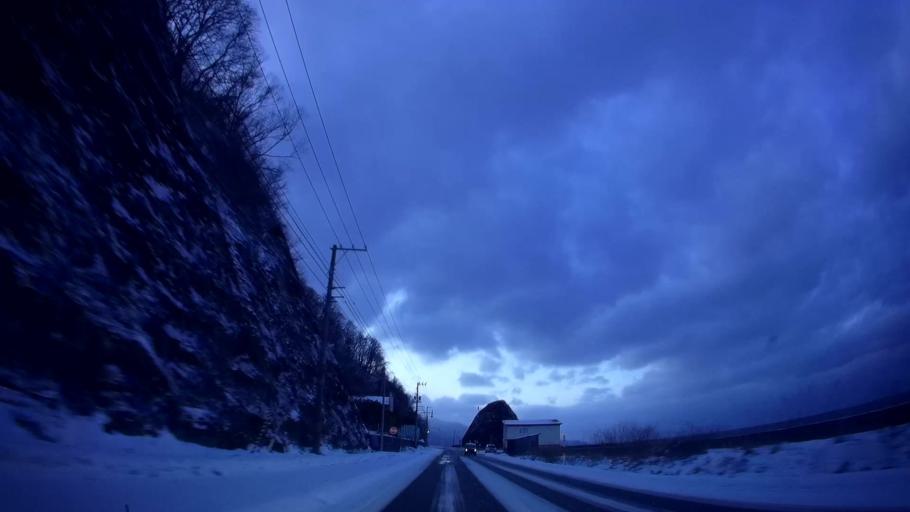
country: JP
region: Hokkaido
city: Hakodate
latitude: 41.8924
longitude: 141.0483
